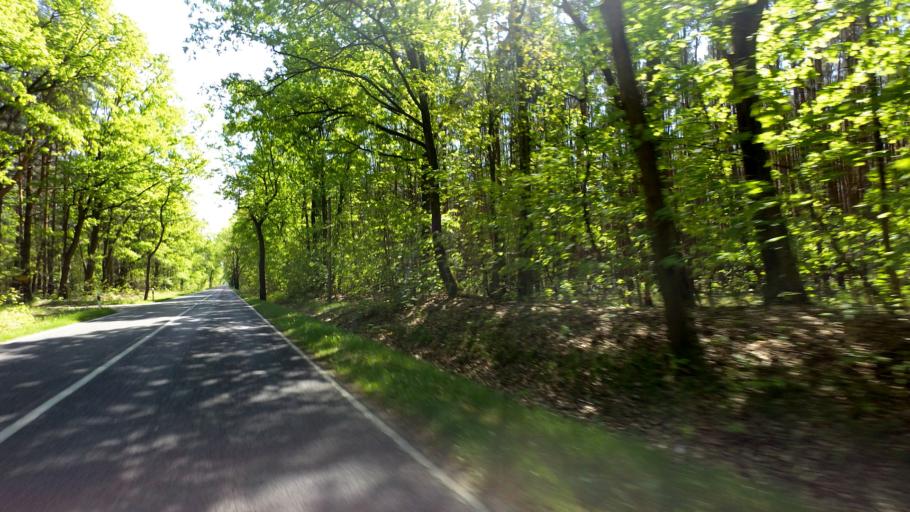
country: DE
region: Brandenburg
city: Bestensee
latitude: 52.2283
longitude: 13.6709
